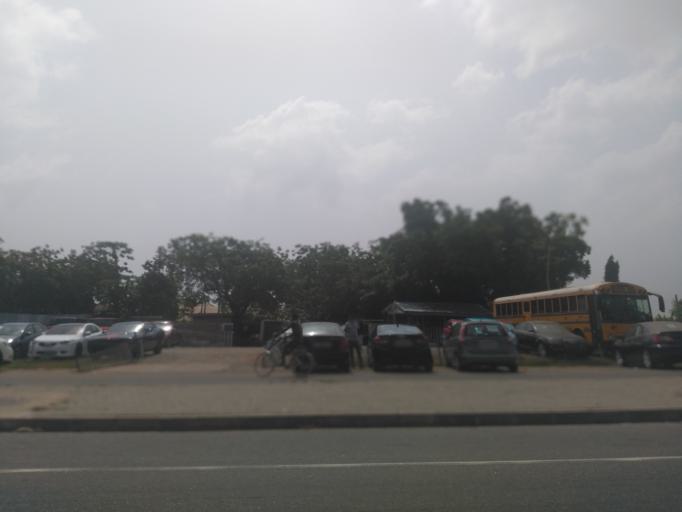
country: GH
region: Greater Accra
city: Dome
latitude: 5.6161
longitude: -0.2055
